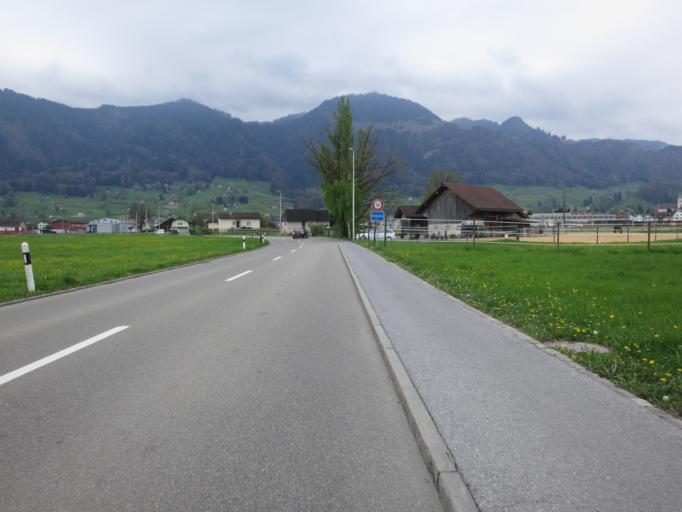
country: CH
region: Schwyz
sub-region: Bezirk March
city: Reichenburg
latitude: 47.1750
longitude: 8.9861
